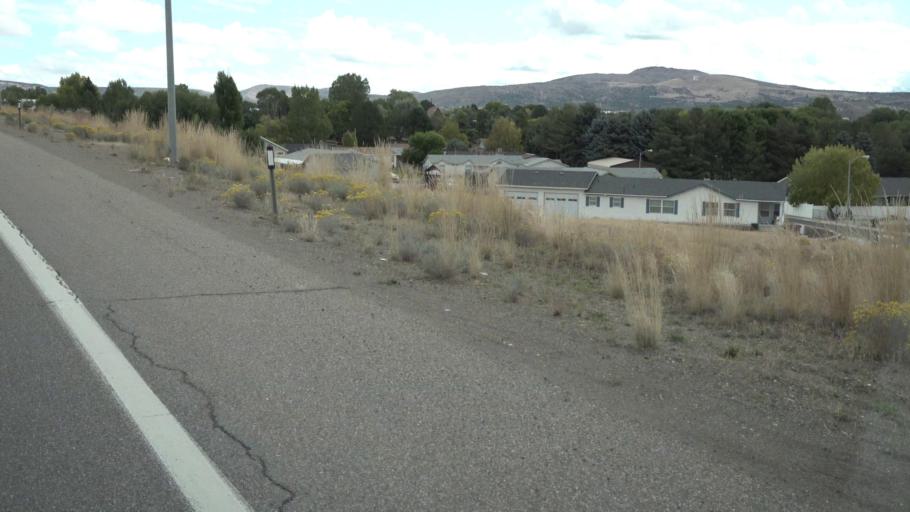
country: US
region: Nevada
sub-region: Elko County
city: Elko
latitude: 40.8366
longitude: -115.7836
